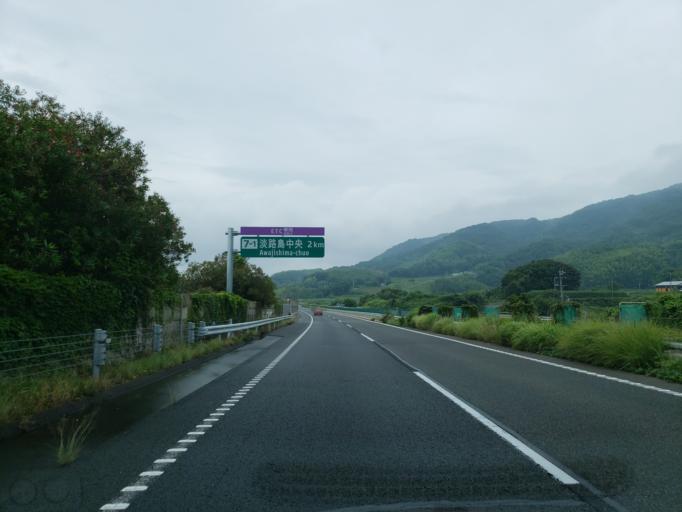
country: JP
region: Hyogo
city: Sumoto
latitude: 34.3926
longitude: 134.8593
